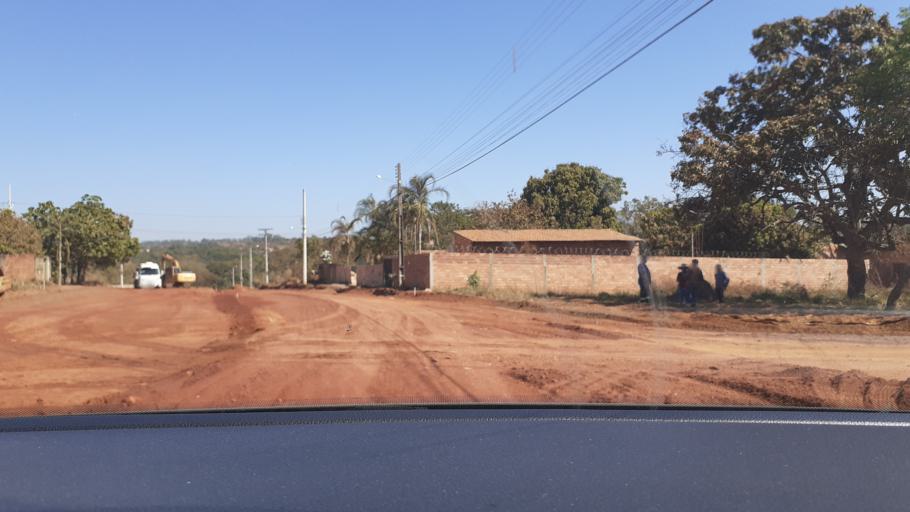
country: BR
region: Goias
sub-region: Aparecida De Goiania
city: Aparecida de Goiania
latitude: -16.8778
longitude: -49.2595
